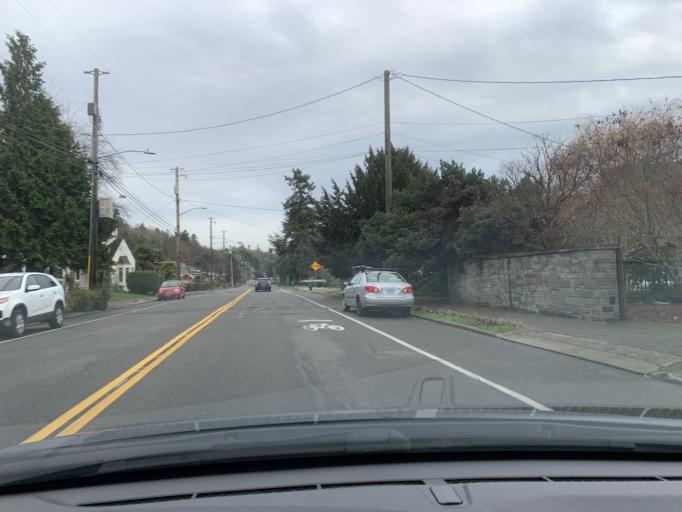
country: US
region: Washington
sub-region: King County
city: White Center
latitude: 47.5595
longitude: -122.4027
